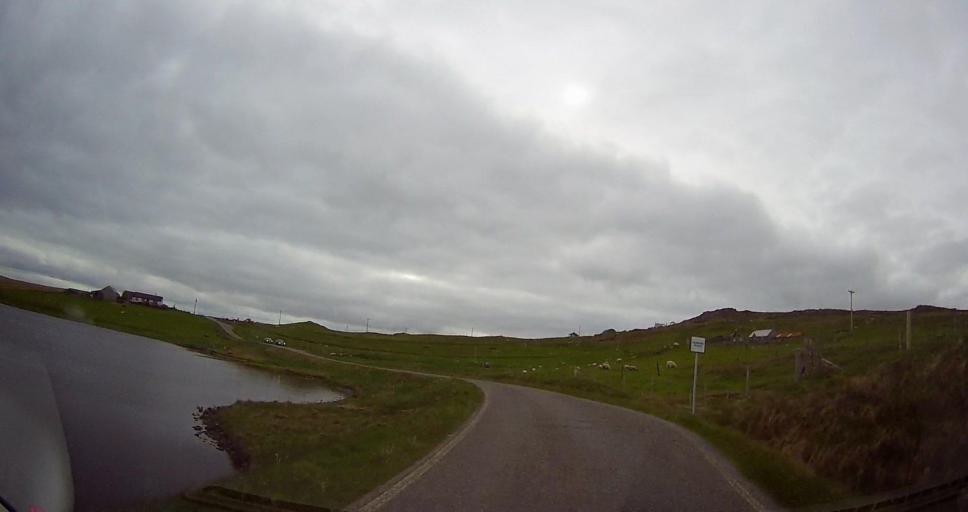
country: GB
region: Scotland
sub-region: Shetland Islands
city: Shetland
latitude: 60.5002
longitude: -1.0741
